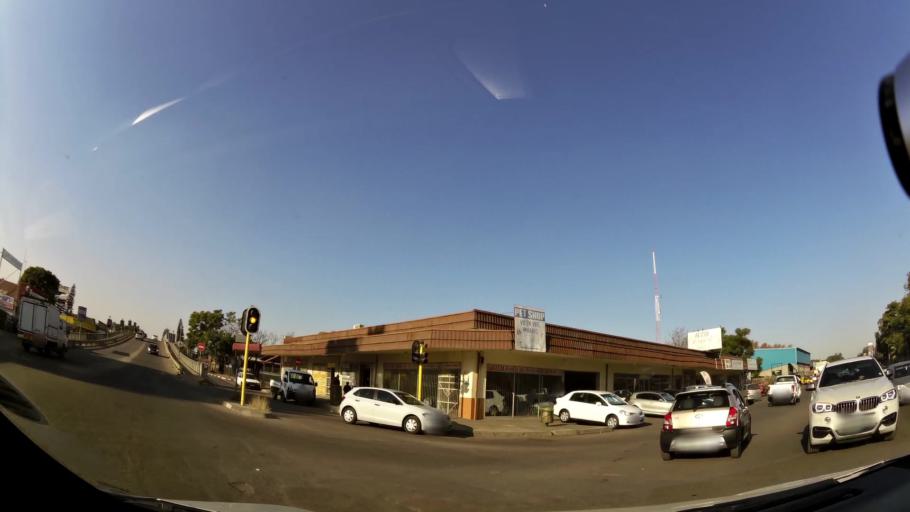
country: ZA
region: North-West
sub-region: Bojanala Platinum District Municipality
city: Rustenburg
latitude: -25.6621
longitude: 27.2469
